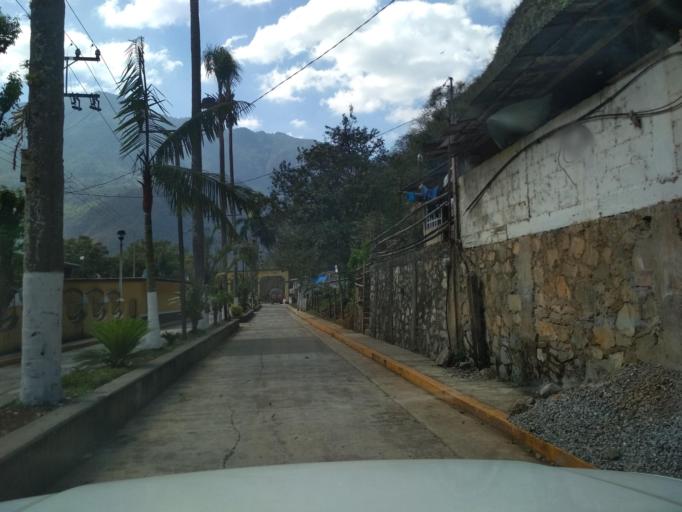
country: MX
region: Veracruz
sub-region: Tlilapan
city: Tonalixco
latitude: 18.7900
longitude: -97.0936
